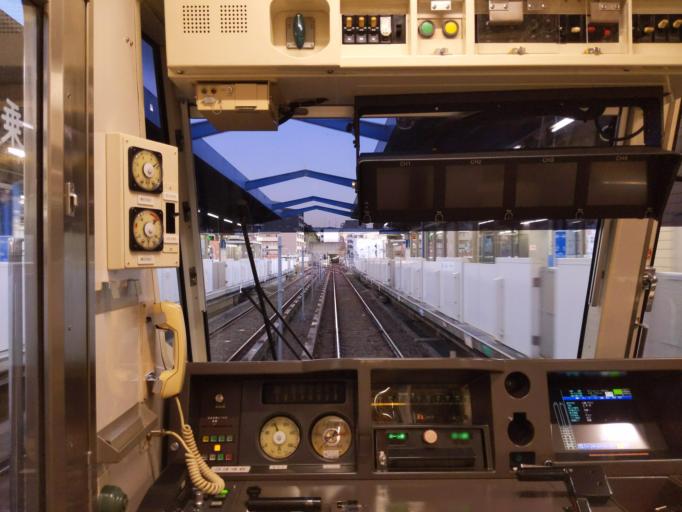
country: JP
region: Kanagawa
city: Yokohama
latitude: 35.4013
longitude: 139.5728
